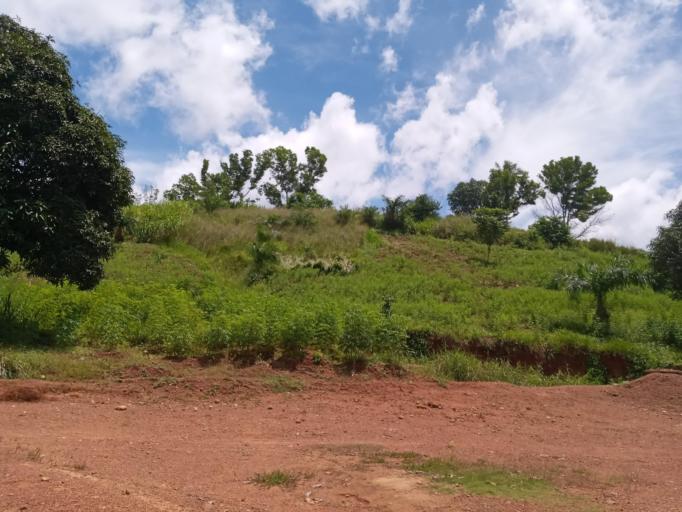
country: SL
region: Eastern Province
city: Tombu
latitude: 8.6286
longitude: -10.8224
